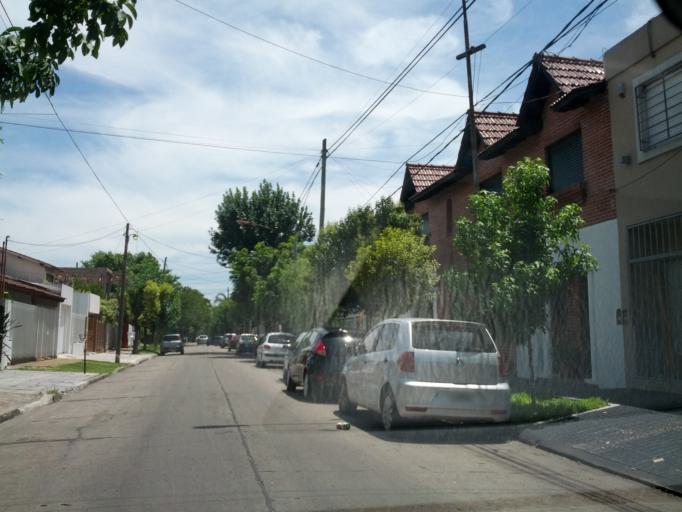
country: AR
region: Buenos Aires
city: San Justo
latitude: -34.6468
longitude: -58.5736
